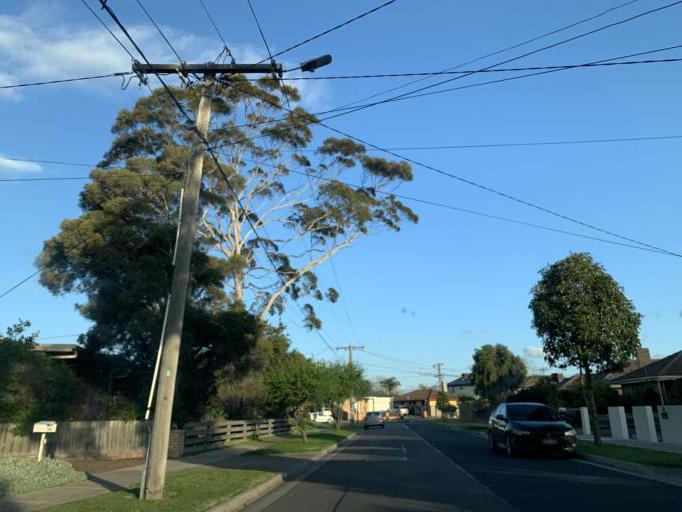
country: AU
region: Victoria
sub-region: Kingston
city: Mordialloc
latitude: -37.9832
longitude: 145.0890
